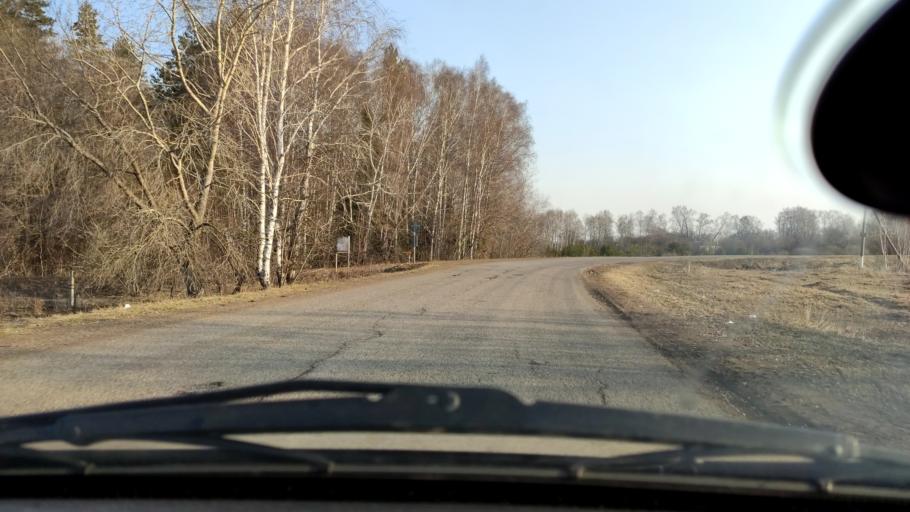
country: RU
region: Bashkortostan
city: Asanovo
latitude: 54.7728
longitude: 55.4885
